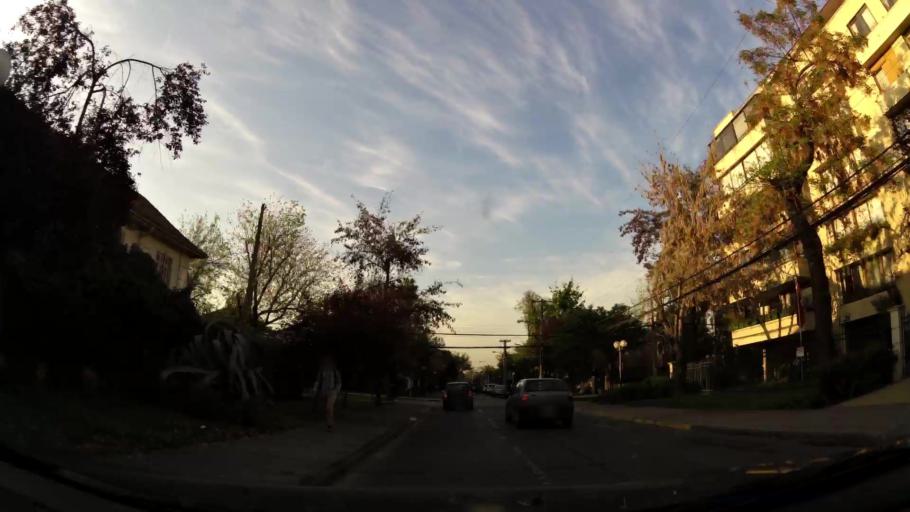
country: CL
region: Santiago Metropolitan
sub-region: Provincia de Santiago
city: Villa Presidente Frei, Nunoa, Santiago, Chile
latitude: -33.4385
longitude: -70.5983
